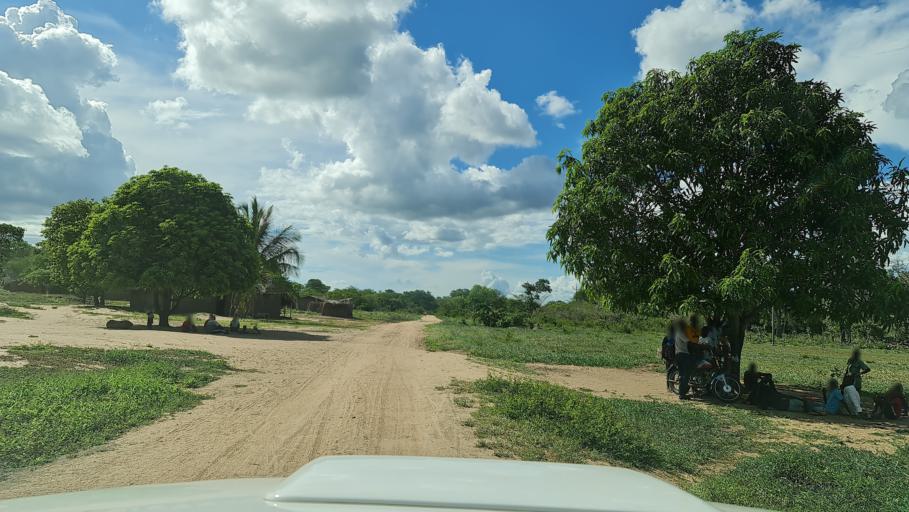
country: MZ
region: Nampula
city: Ilha de Mocambique
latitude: -15.4049
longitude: 40.2407
